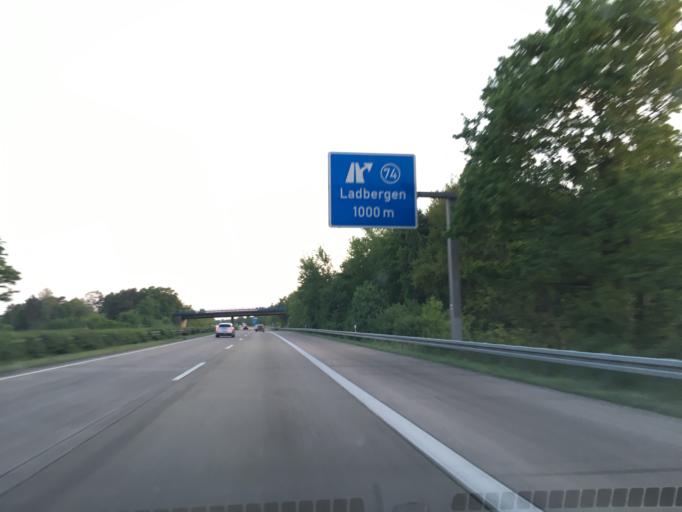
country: DE
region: North Rhine-Westphalia
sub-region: Regierungsbezirk Munster
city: Ladbergen
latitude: 52.1578
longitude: 7.7433
